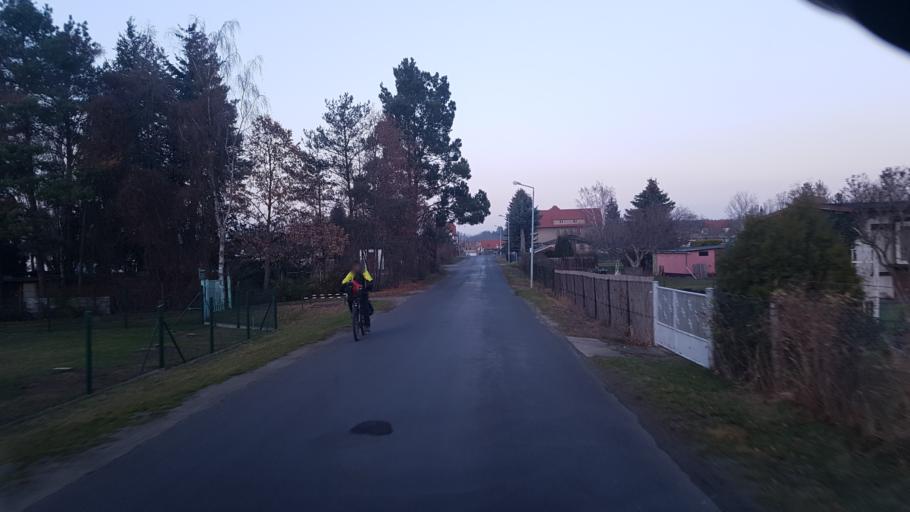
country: DE
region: Brandenburg
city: Lauchhammer
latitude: 51.5084
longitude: 13.7559
